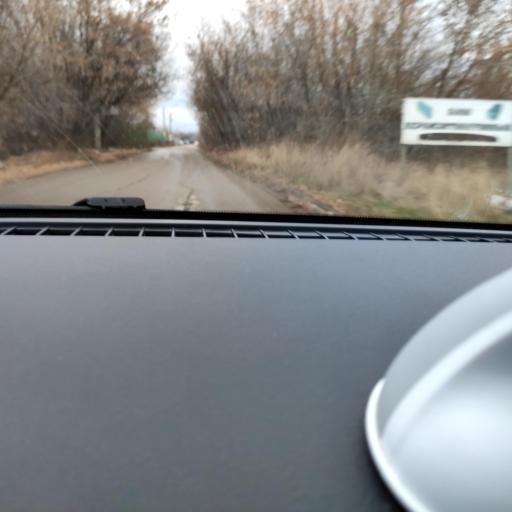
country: RU
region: Samara
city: Petra-Dubrava
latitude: 53.2602
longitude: 50.2978
